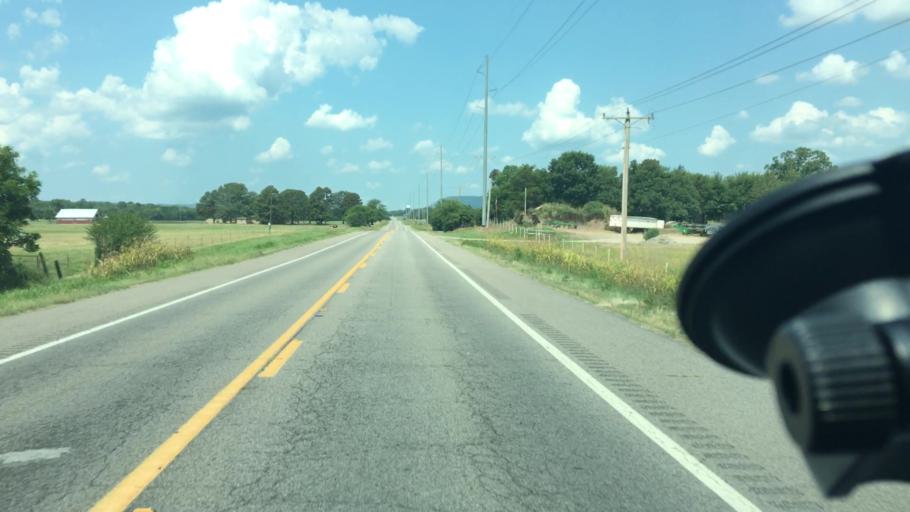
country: US
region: Arkansas
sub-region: Logan County
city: Paris
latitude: 35.2948
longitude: -93.6631
